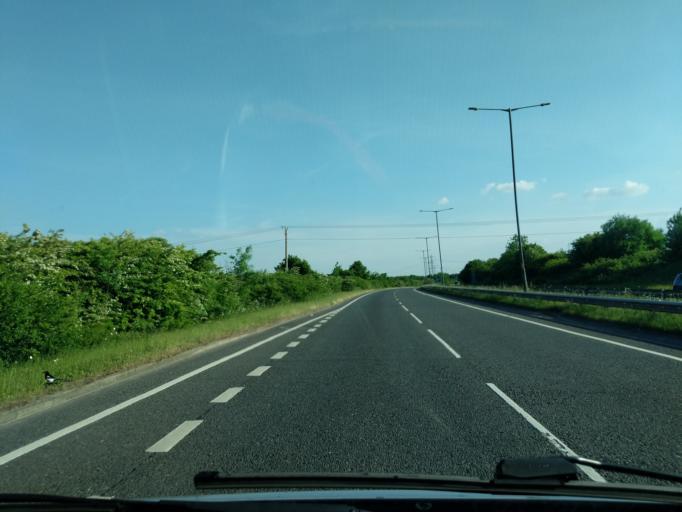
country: GB
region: England
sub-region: St. Helens
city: St Helens
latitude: 53.4109
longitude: -2.7437
